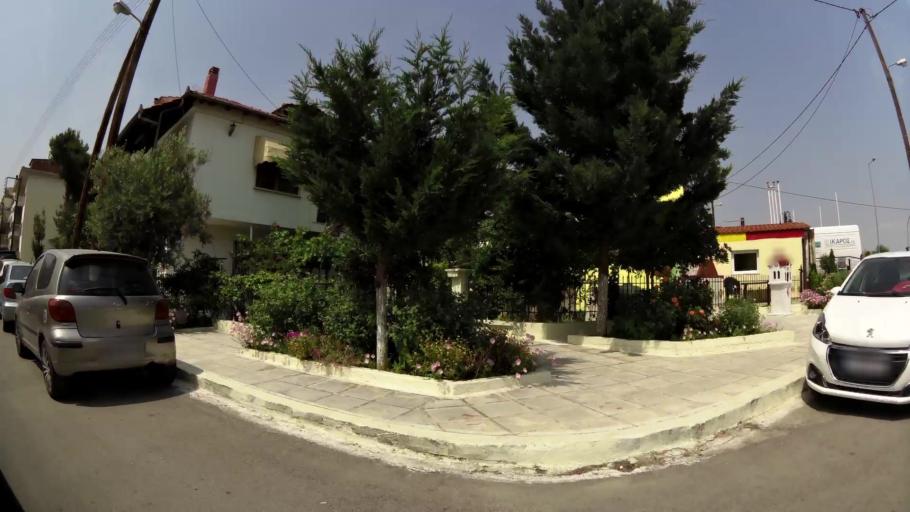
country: GR
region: Central Macedonia
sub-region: Nomos Thessalonikis
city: Diavata
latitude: 40.6901
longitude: 22.8597
